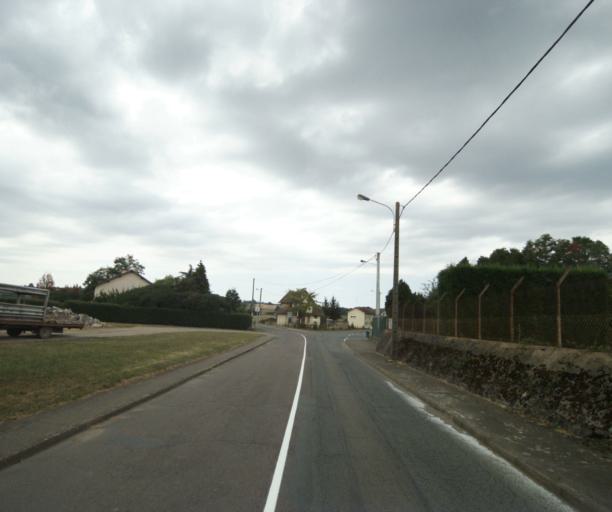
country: FR
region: Bourgogne
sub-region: Departement de Saone-et-Loire
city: Gueugnon
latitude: 46.6086
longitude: 4.0615
